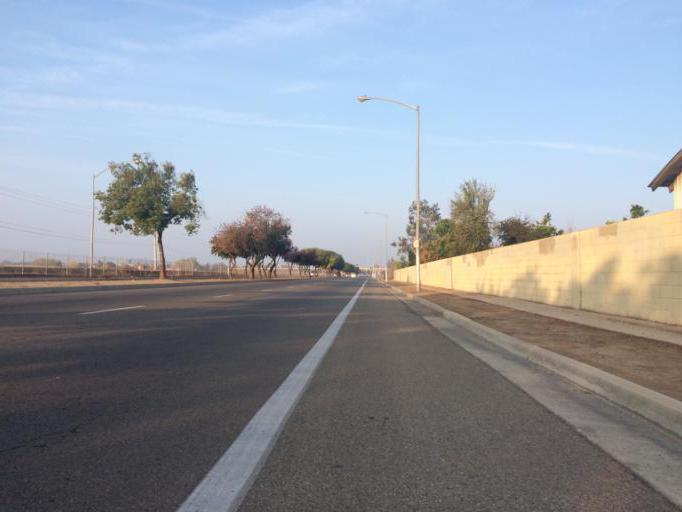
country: US
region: California
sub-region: Fresno County
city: Tarpey Village
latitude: 36.7944
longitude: -119.7395
